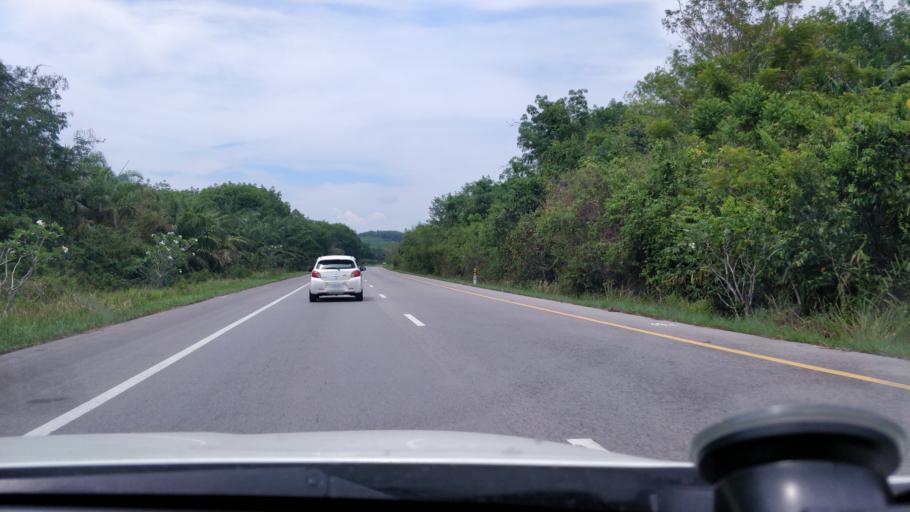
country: TH
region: Surat Thani
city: Khian Sa
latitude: 8.8014
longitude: 99.1626
